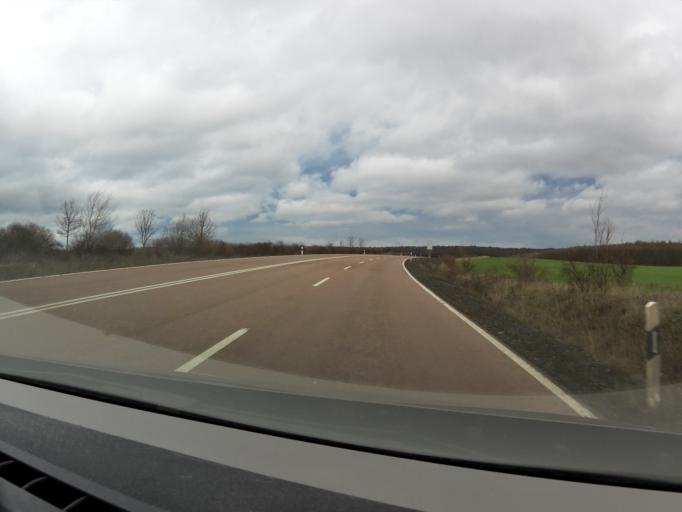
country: DE
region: Saxony-Anhalt
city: Riestedt
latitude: 51.5159
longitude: 11.3764
